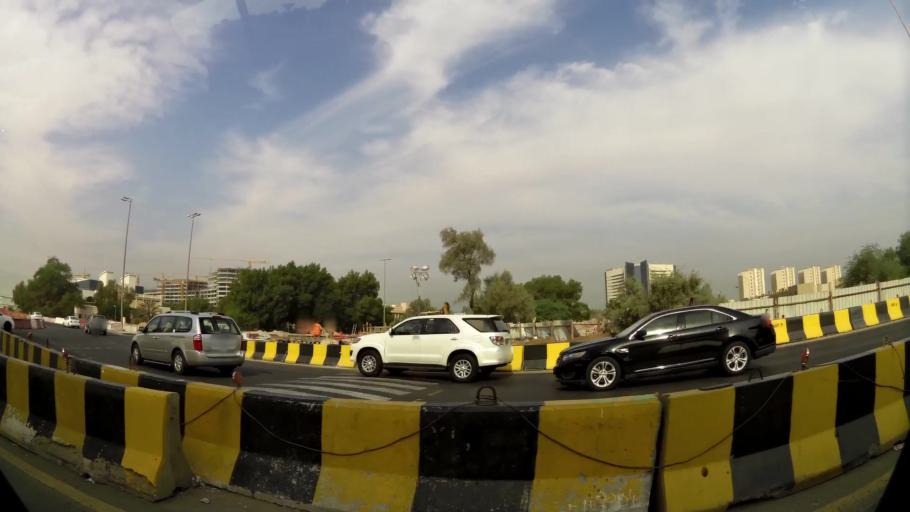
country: KW
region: Al Asimah
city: Ar Rabiyah
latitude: 29.3326
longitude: 47.9089
